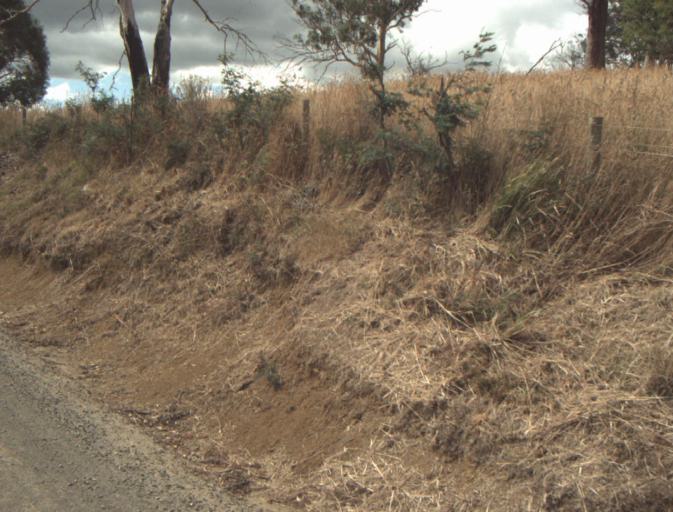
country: AU
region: Tasmania
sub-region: Launceston
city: Mayfield
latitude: -41.3074
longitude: 146.9962
